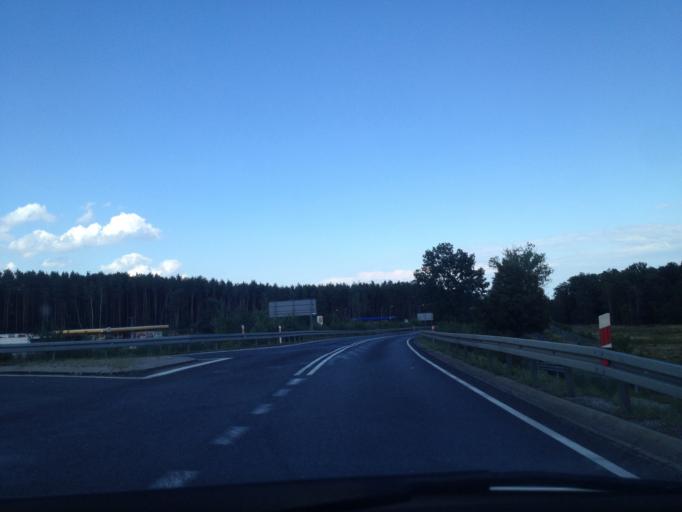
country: PL
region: Lubusz
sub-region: Powiat zaganski
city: Ilowa
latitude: 51.5242
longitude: 15.2191
